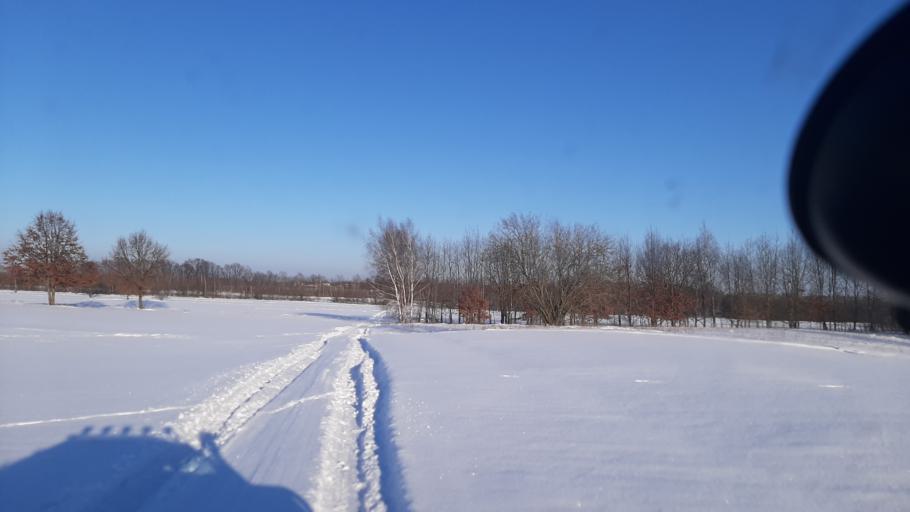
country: PL
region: Lublin Voivodeship
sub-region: Powiat lubelski
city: Jastkow
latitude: 51.3863
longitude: 22.4295
